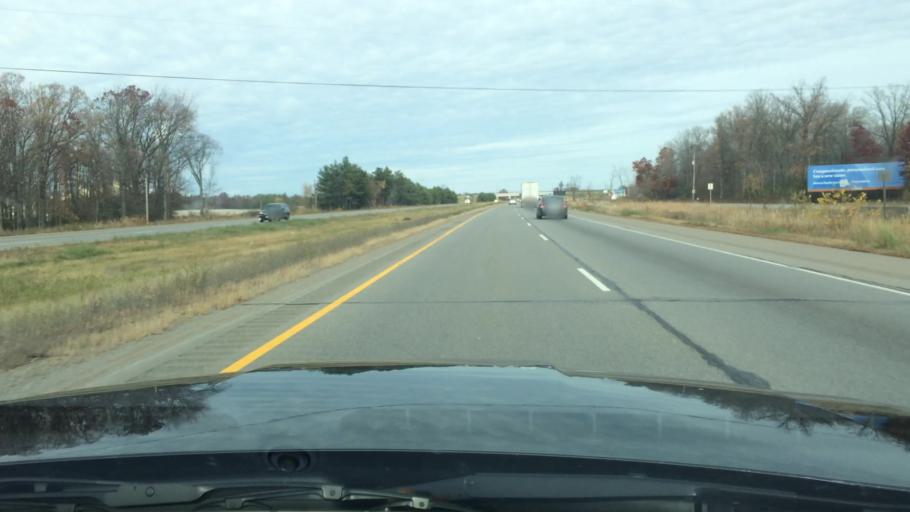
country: US
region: Wisconsin
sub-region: Marathon County
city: Evergreen
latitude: 44.8364
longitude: -89.6524
